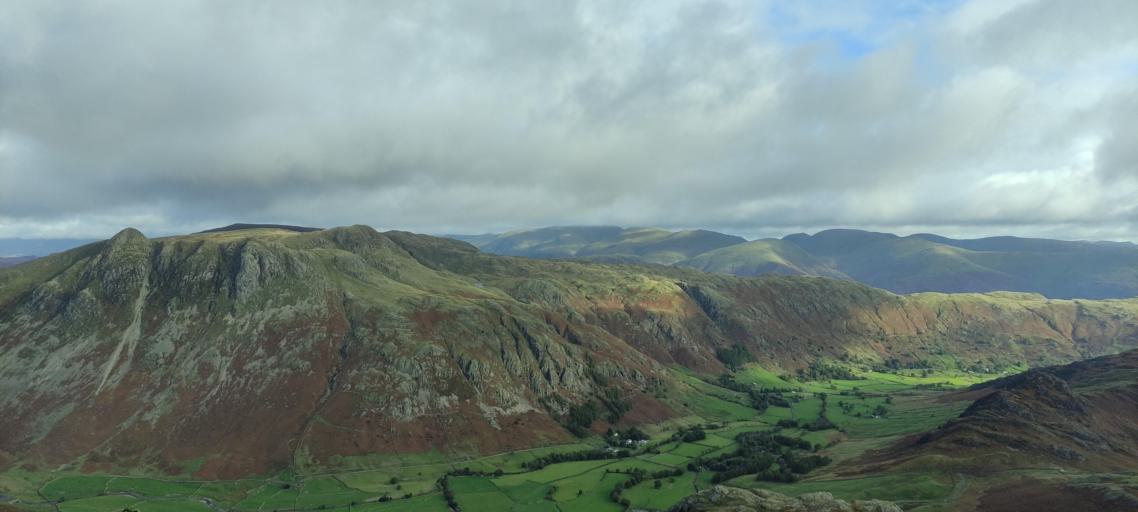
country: GB
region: England
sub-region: Cumbria
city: Ambleside
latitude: 54.4279
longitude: -3.1234
